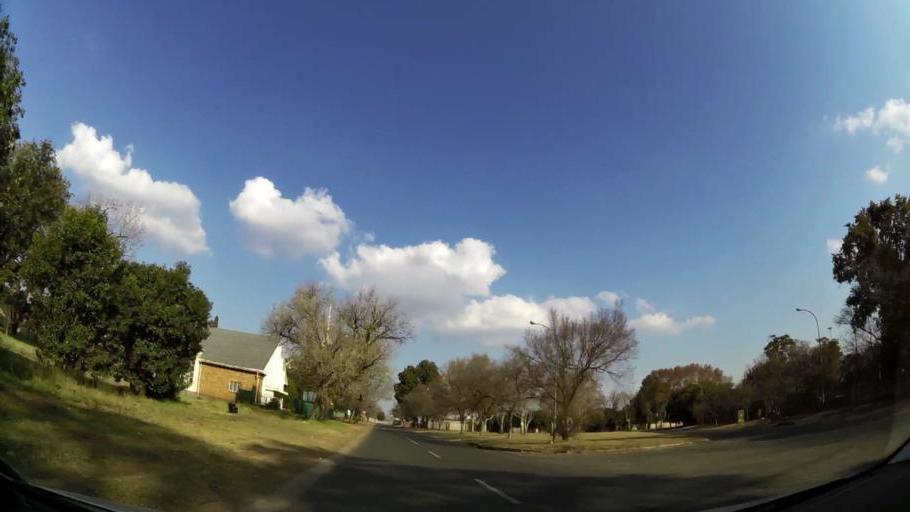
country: ZA
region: Gauteng
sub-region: Ekurhuleni Metropolitan Municipality
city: Tembisa
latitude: -25.9543
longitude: 28.2299
